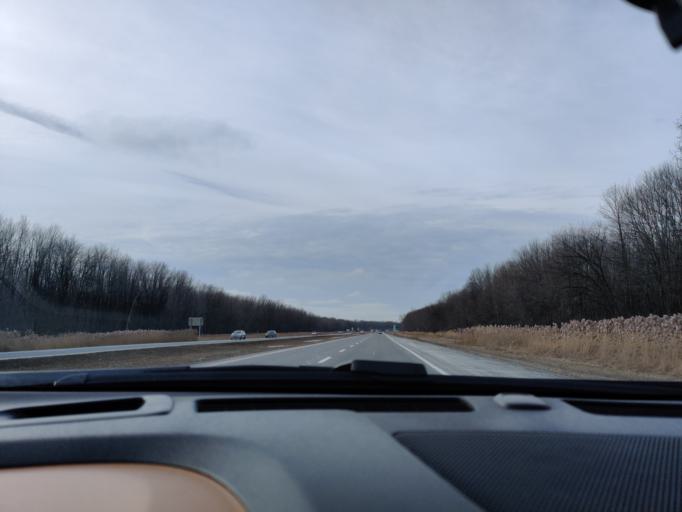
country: CA
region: Quebec
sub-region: Monteregie
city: Les Coteaux
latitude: 45.2317
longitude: -74.2957
